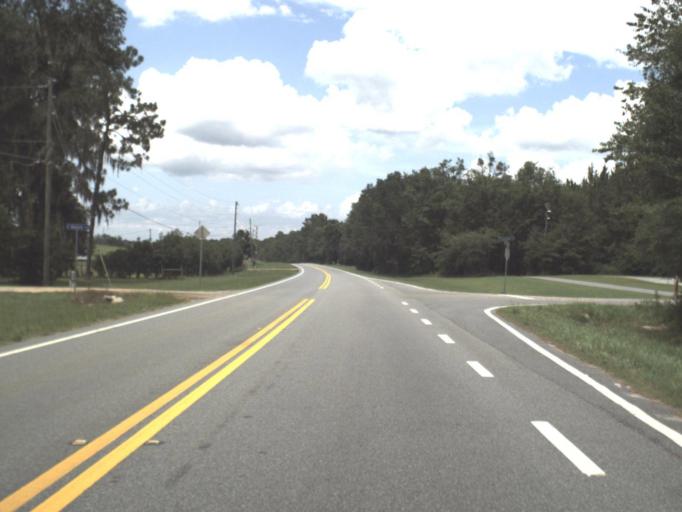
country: US
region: Florida
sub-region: Madison County
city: Madison
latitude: 30.5194
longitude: -83.3693
